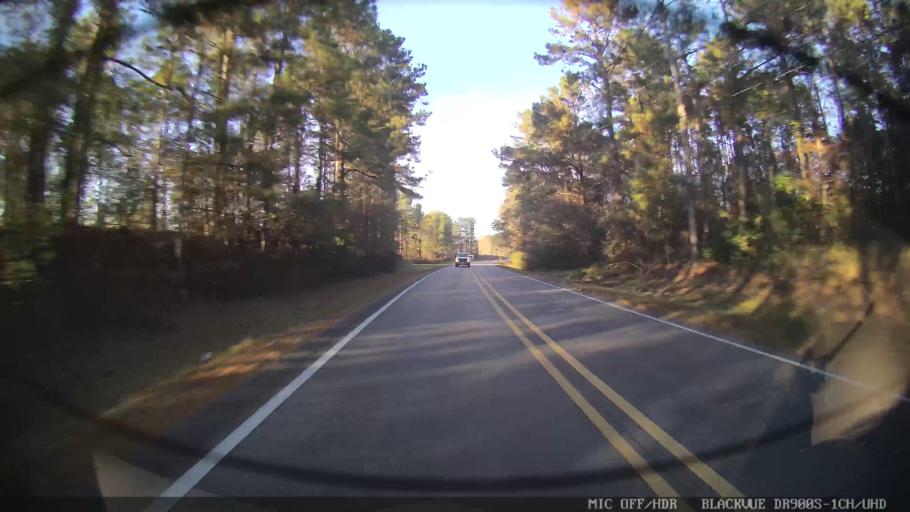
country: US
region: Mississippi
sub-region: Lamar County
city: Lumberton
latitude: 31.0193
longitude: -89.4505
